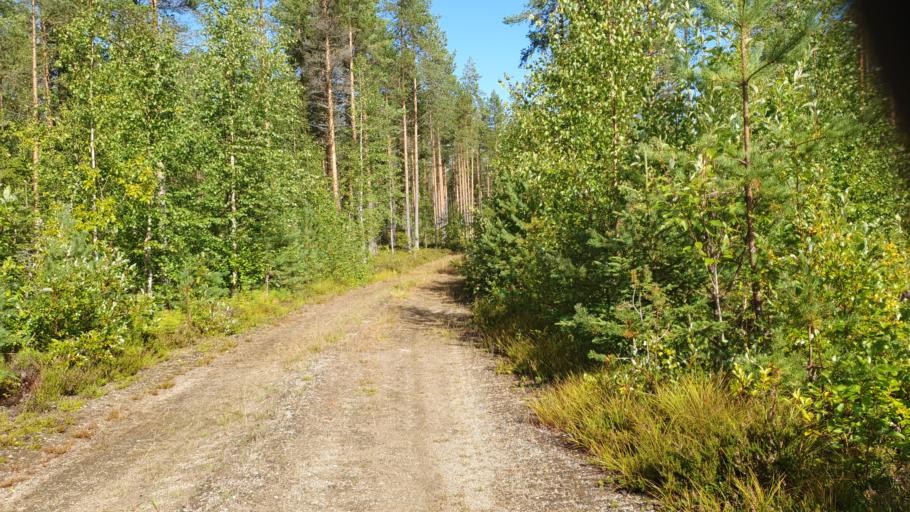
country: FI
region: Kainuu
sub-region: Kehys-Kainuu
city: Kuhmo
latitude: 64.1305
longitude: 29.3795
